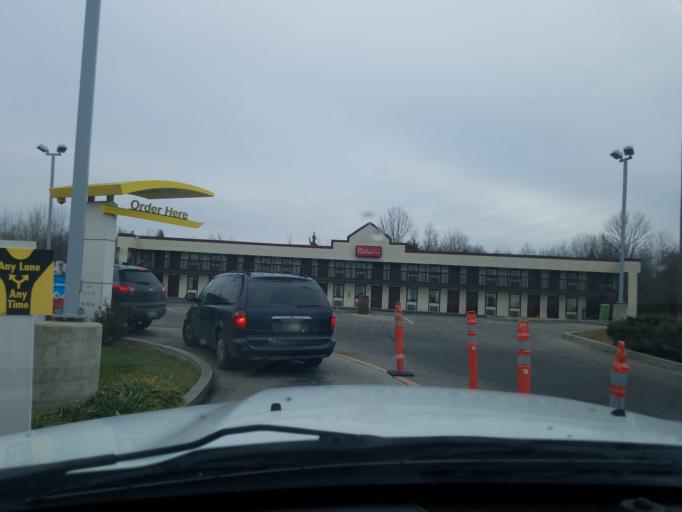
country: US
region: Indiana
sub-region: Scott County
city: Scottsburg
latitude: 38.6859
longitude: -85.7921
